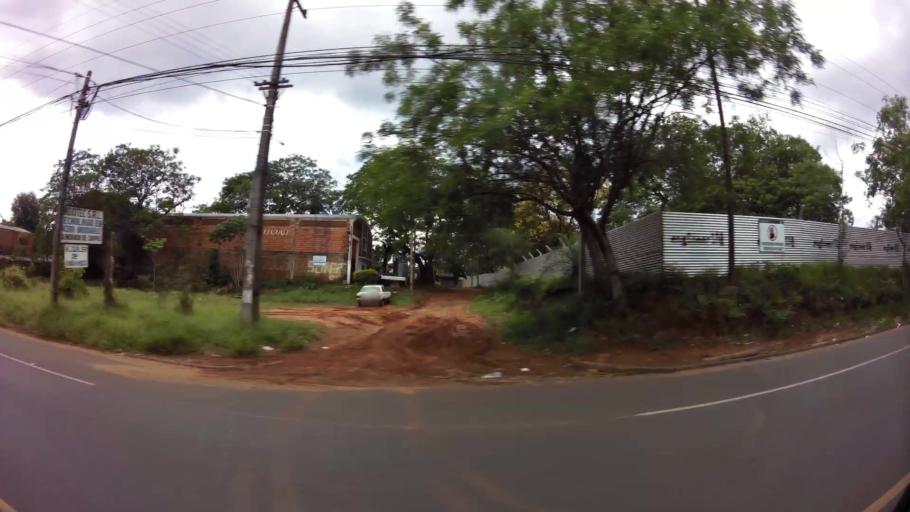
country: PY
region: Central
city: San Lorenzo
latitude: -25.2840
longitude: -57.4991
